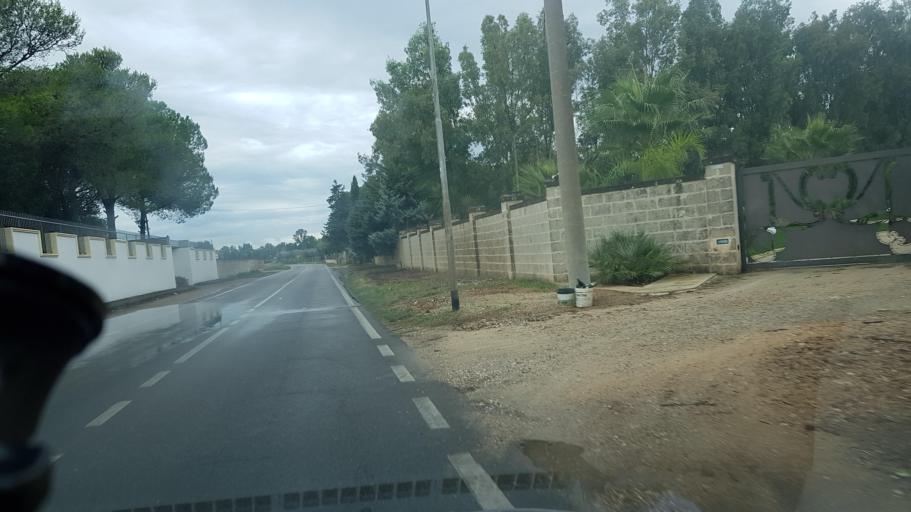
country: IT
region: Apulia
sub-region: Provincia di Lecce
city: Carmiano
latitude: 40.3534
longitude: 18.0307
